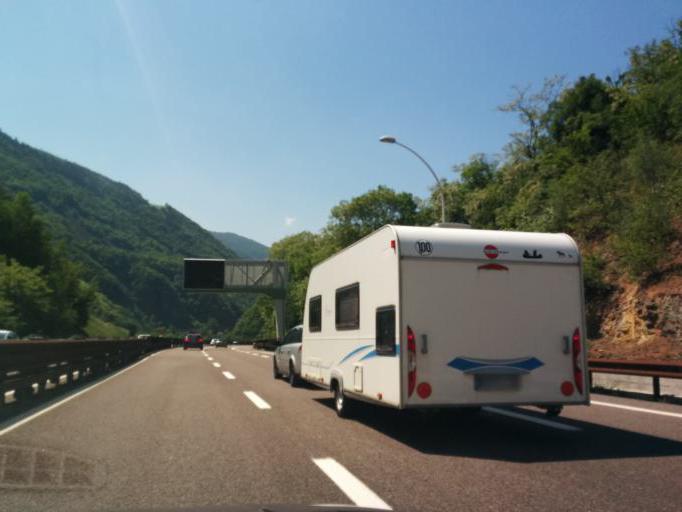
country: IT
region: Trentino-Alto Adige
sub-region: Bolzano
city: Fie Allo Sciliar
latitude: 46.5295
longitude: 11.4905
